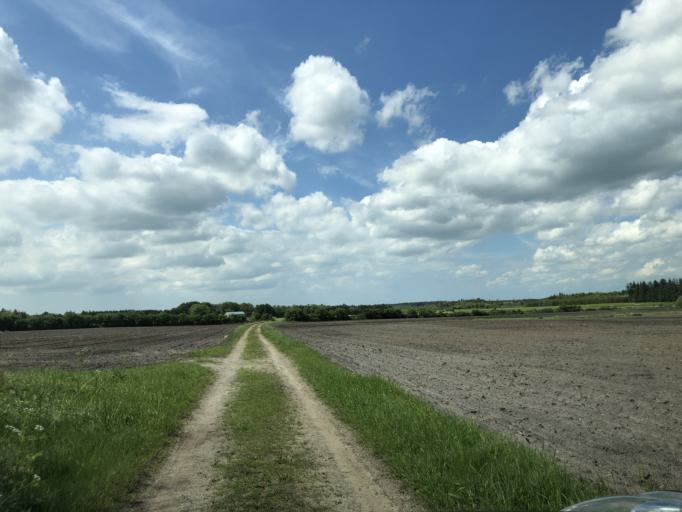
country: DK
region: Central Jutland
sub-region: Holstebro Kommune
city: Ulfborg
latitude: 56.2423
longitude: 8.4258
